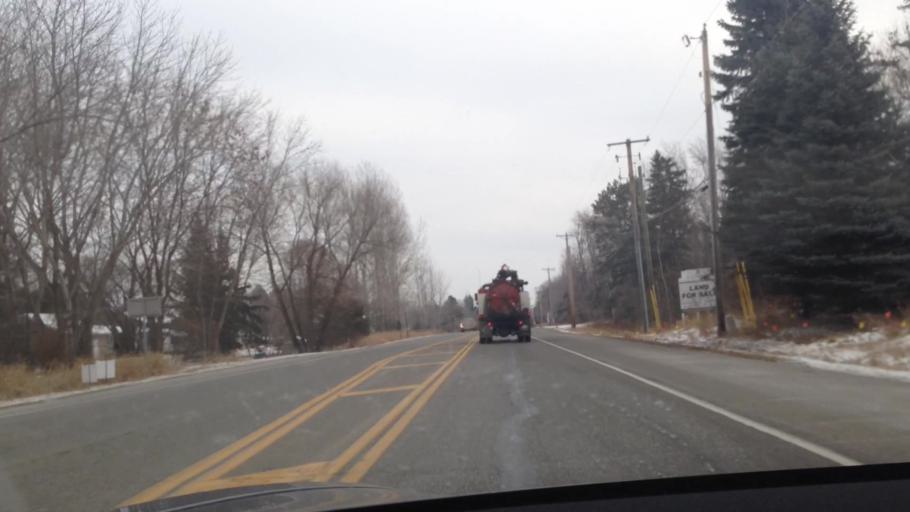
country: US
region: Minnesota
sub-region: Washington County
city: Forest Lake
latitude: 45.2524
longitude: -93.0075
